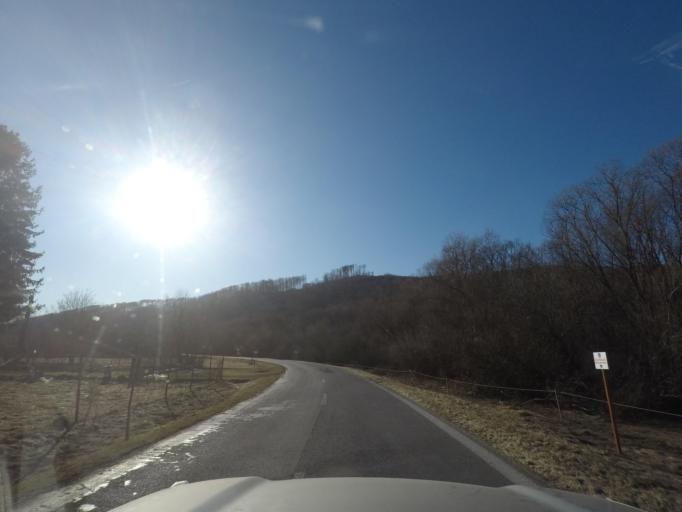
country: SK
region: Presovsky
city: Medzilaborce
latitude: 49.1661
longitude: 22.0243
